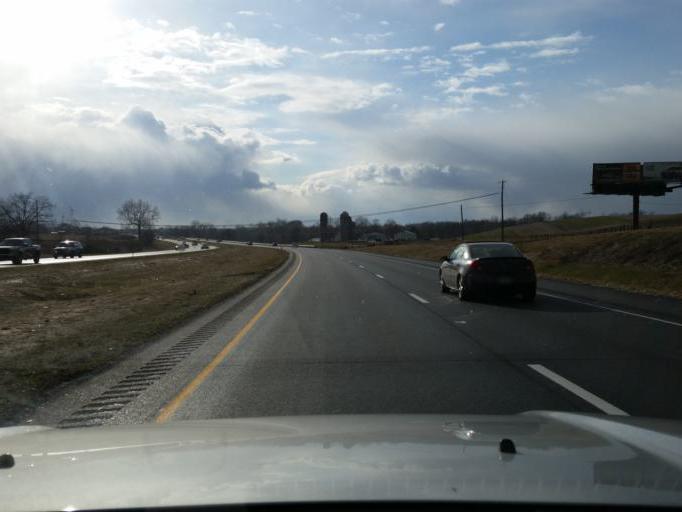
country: US
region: Pennsylvania
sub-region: Lancaster County
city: Mount Joy
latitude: 40.1307
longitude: -76.4848
